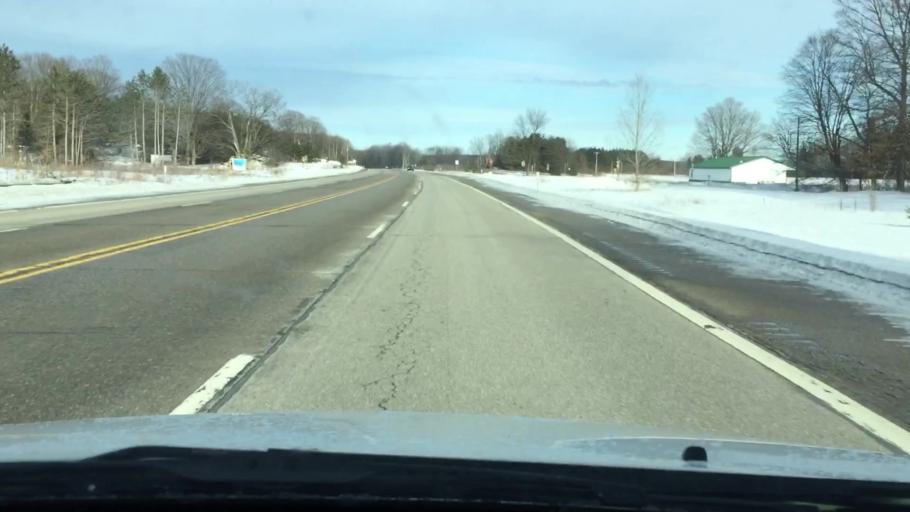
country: US
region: Michigan
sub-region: Kalkaska County
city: Kalkaska
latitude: 44.6101
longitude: -85.3137
